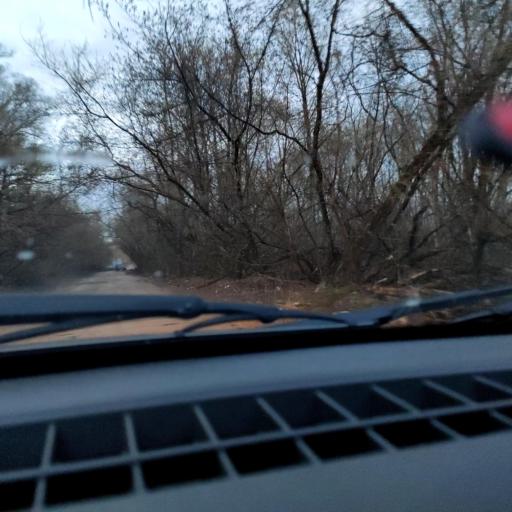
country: RU
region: Bashkortostan
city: Ufa
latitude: 54.6771
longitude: 55.9754
